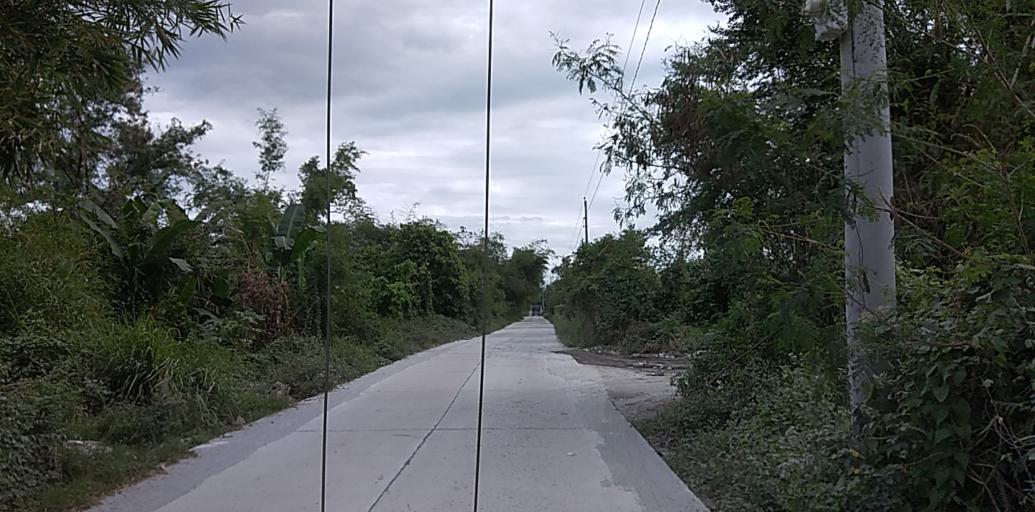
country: PH
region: Central Luzon
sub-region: Province of Pampanga
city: Pulung Santol
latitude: 15.0564
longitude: 120.5579
